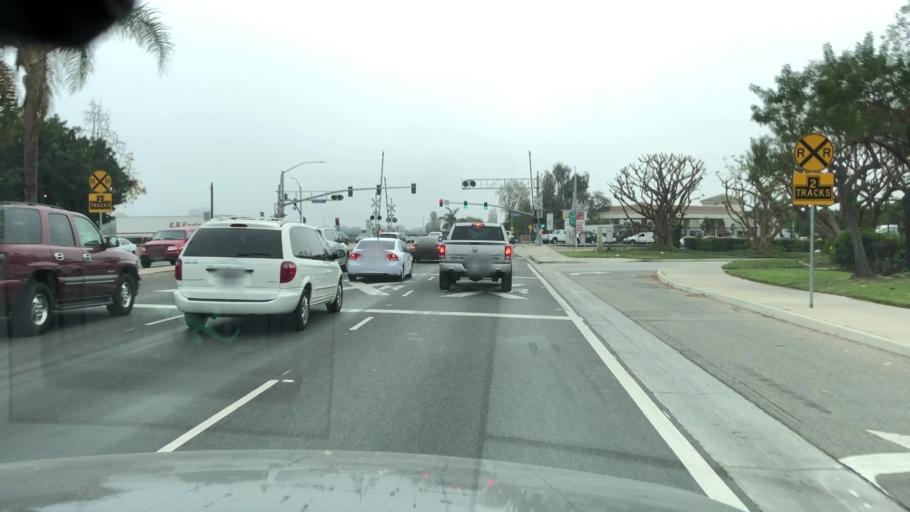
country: US
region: California
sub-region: Ventura County
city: Oxnard
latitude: 34.1981
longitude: -119.1599
